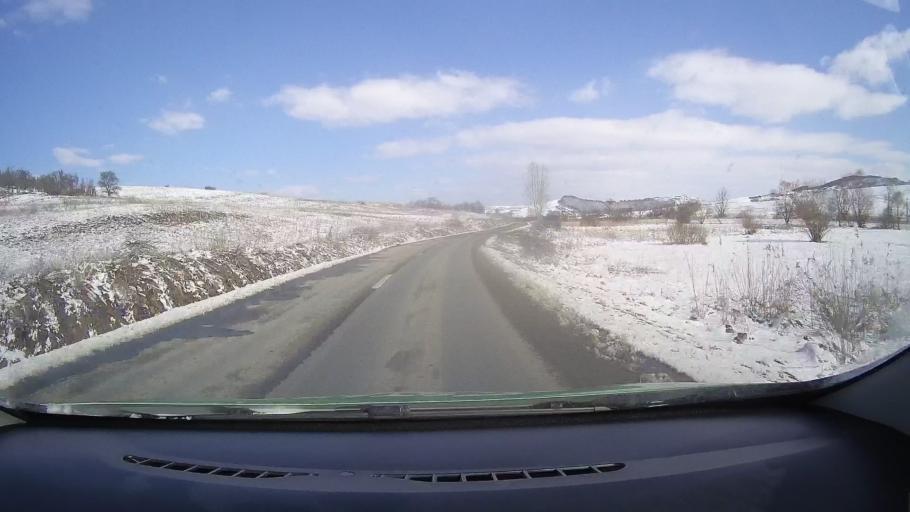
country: RO
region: Sibiu
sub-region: Comuna Altina
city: Altina
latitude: 45.9800
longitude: 24.4688
